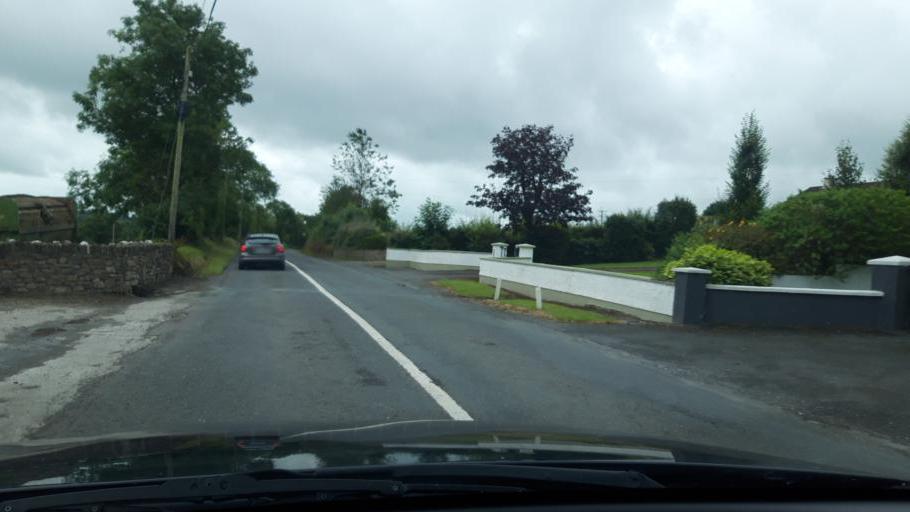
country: IE
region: Munster
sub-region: County Cork
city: Youghal
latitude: 52.1601
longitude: -7.8455
